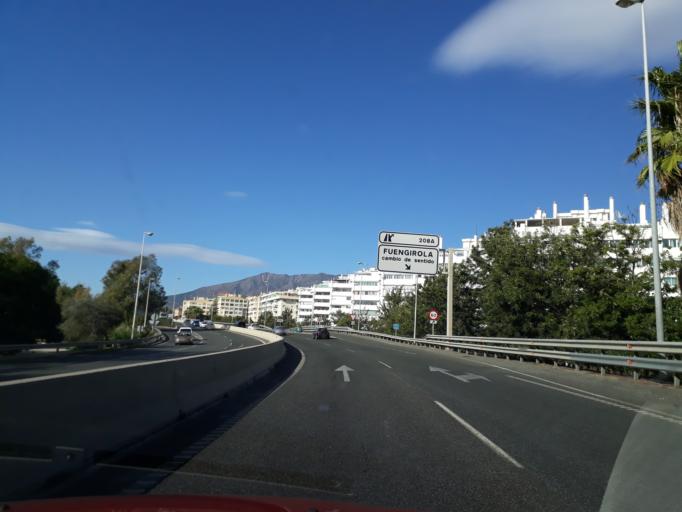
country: ES
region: Andalusia
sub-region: Provincia de Malaga
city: Fuengirola
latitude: 36.5295
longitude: -4.6286
